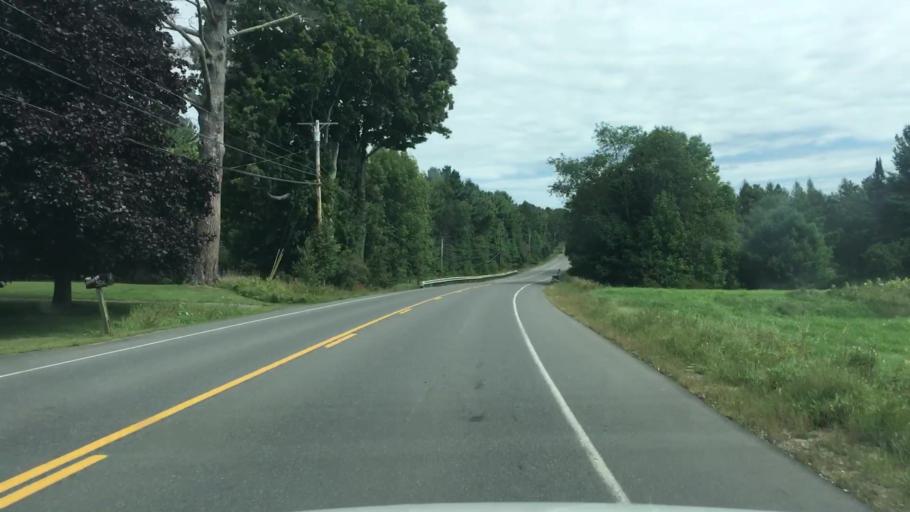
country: US
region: Maine
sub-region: Piscataquis County
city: Dover-Foxcroft
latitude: 45.2058
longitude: -69.1828
